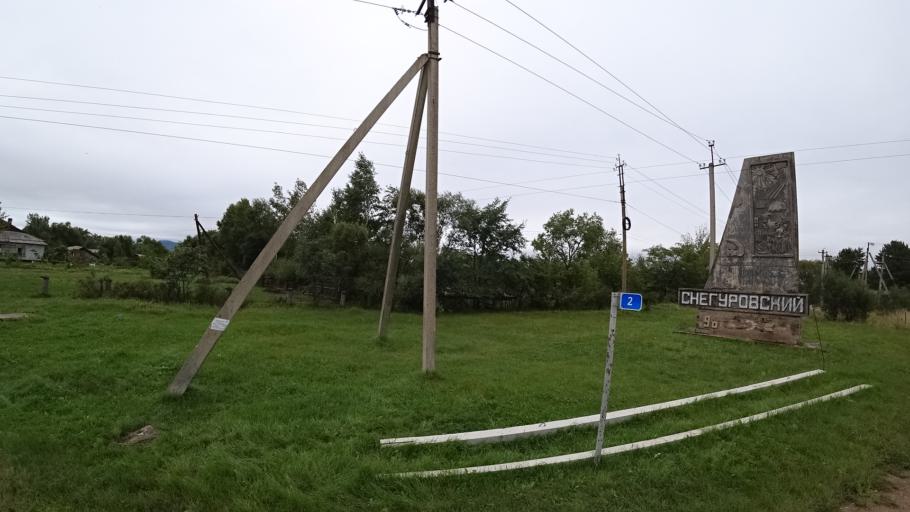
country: RU
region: Primorskiy
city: Monastyrishche
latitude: 44.0775
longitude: 132.5891
